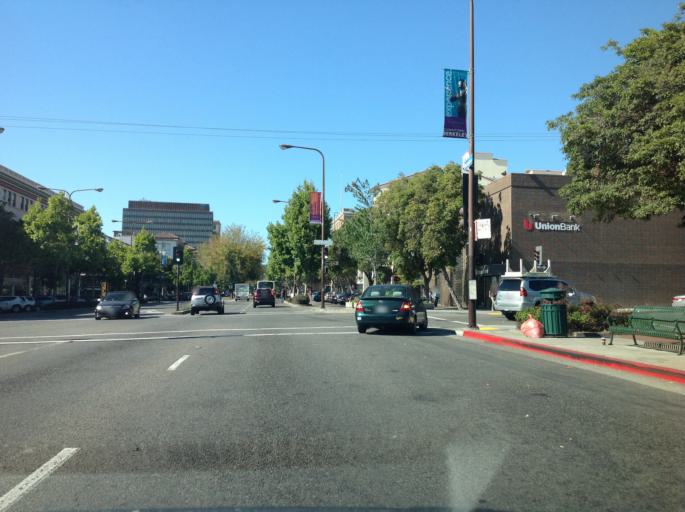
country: US
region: California
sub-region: Alameda County
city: Berkeley
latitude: 37.8664
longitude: -122.2675
